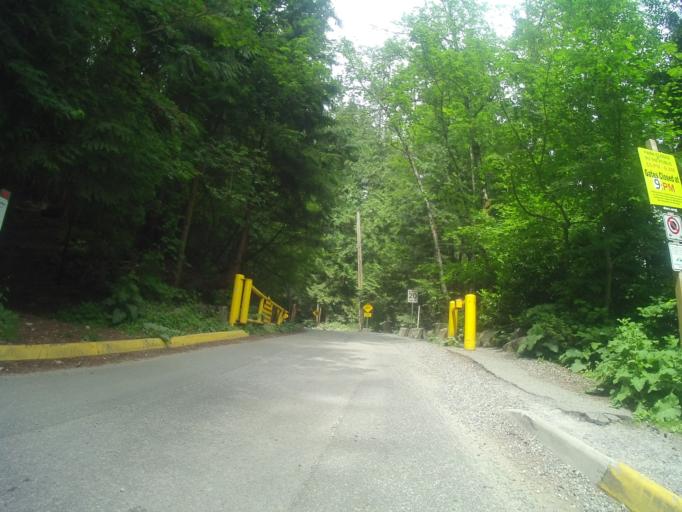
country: CA
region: British Columbia
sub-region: Fraser Valley Regional District
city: North Vancouver
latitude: 49.3551
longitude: -123.0371
